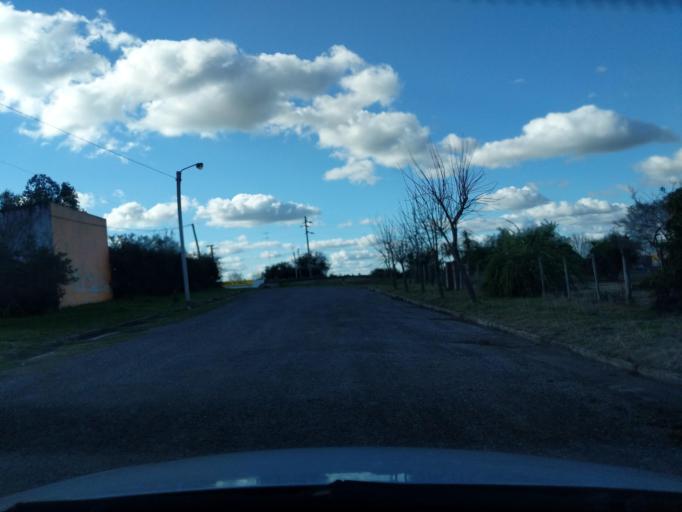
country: UY
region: Florida
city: Florida
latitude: -34.0869
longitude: -56.2107
